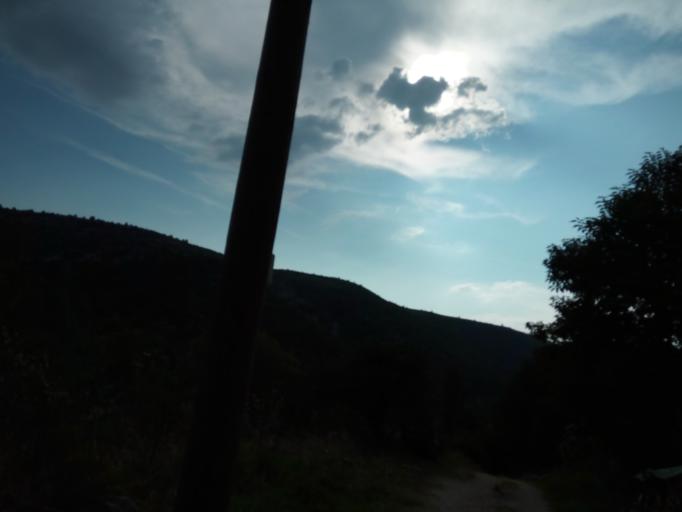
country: HR
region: Sibensko-Kniniska
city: Kistanje
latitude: 43.9063
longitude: 15.9728
